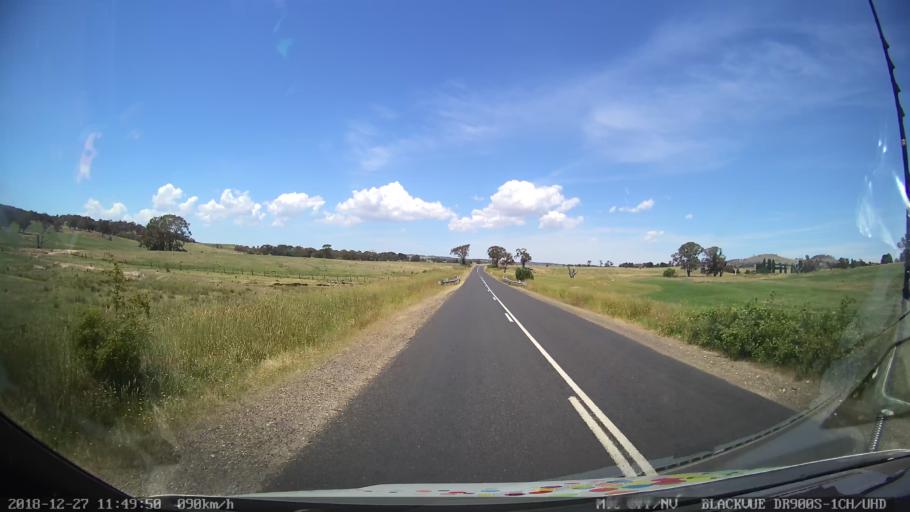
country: AU
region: New South Wales
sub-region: Bathurst Regional
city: Perthville
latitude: -33.6257
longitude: 149.4349
